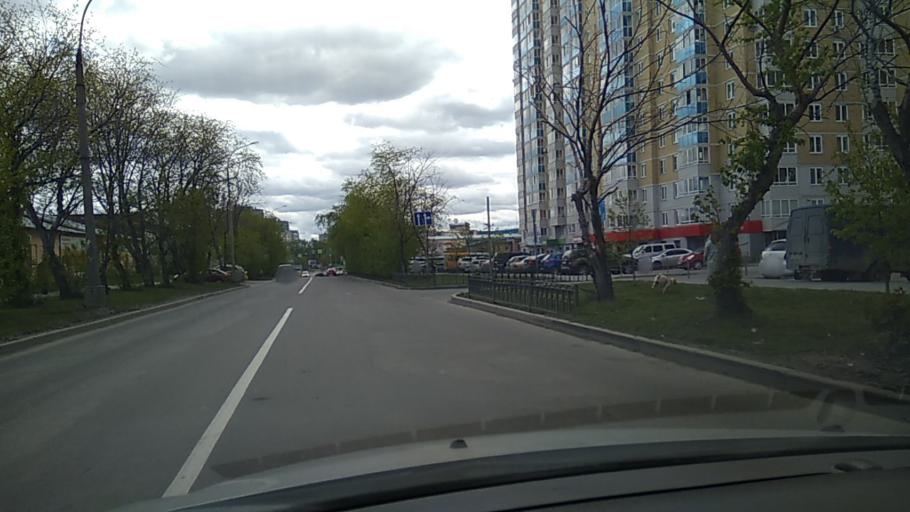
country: RU
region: Sverdlovsk
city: Yekaterinburg
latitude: 56.8336
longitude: 60.6624
